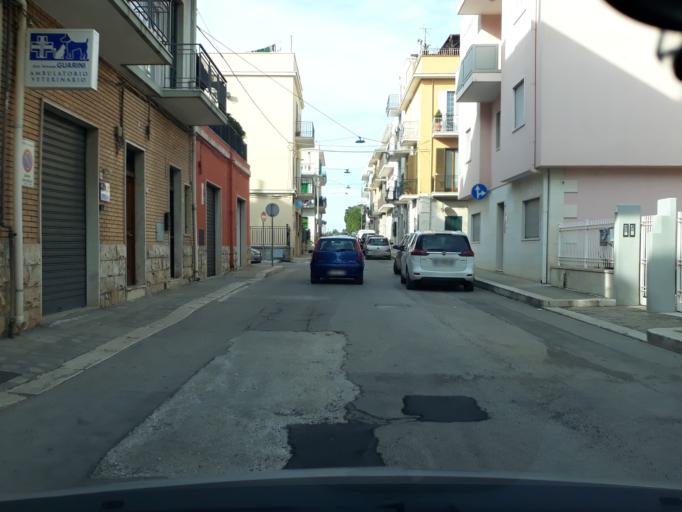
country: IT
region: Apulia
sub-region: Provincia di Brindisi
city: Fasano
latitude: 40.8317
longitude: 17.3547
